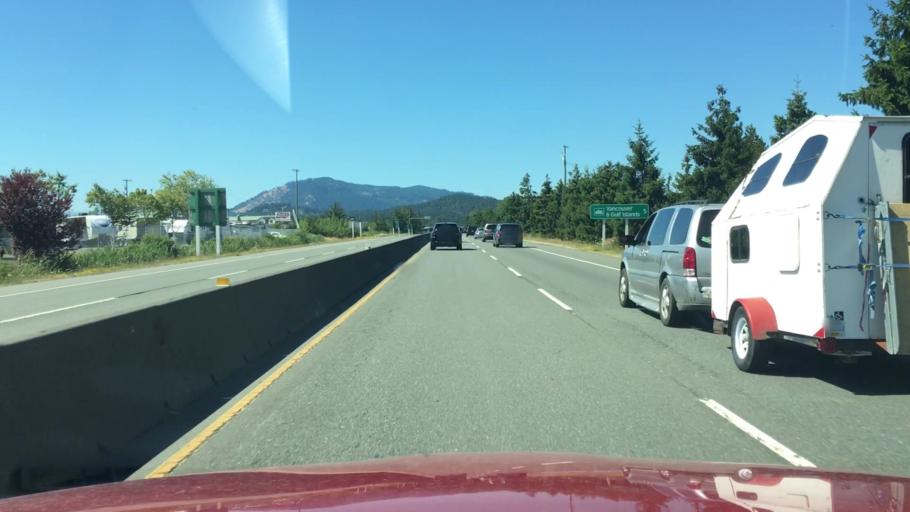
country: CA
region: British Columbia
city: North Saanich
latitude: 48.6541
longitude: -123.4109
